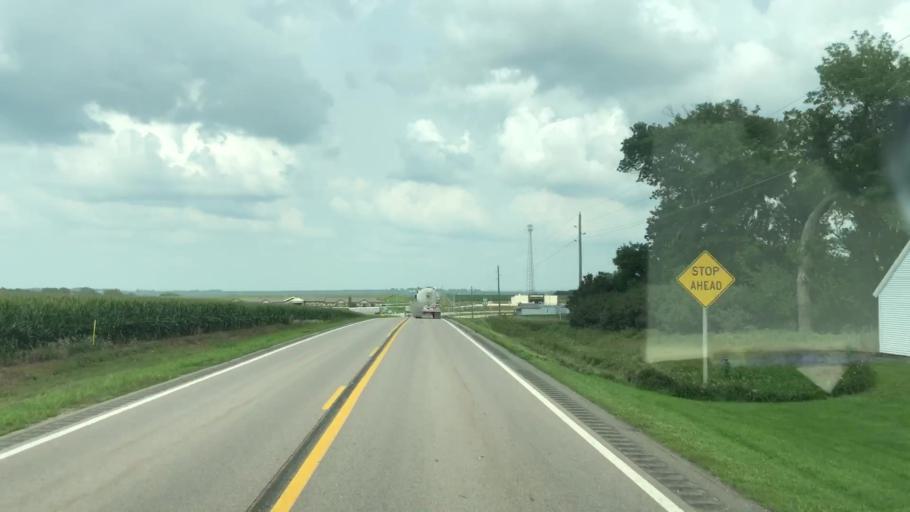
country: US
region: Iowa
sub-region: Plymouth County
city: Remsen
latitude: 42.8040
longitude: -95.9577
